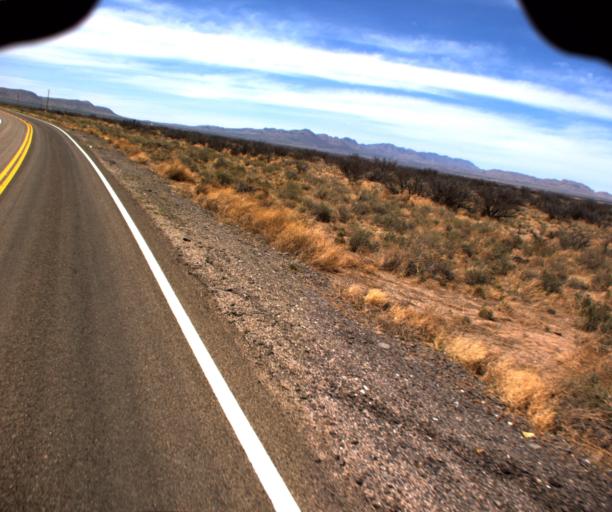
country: US
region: Arizona
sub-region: Cochise County
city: Willcox
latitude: 32.1382
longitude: -109.9155
